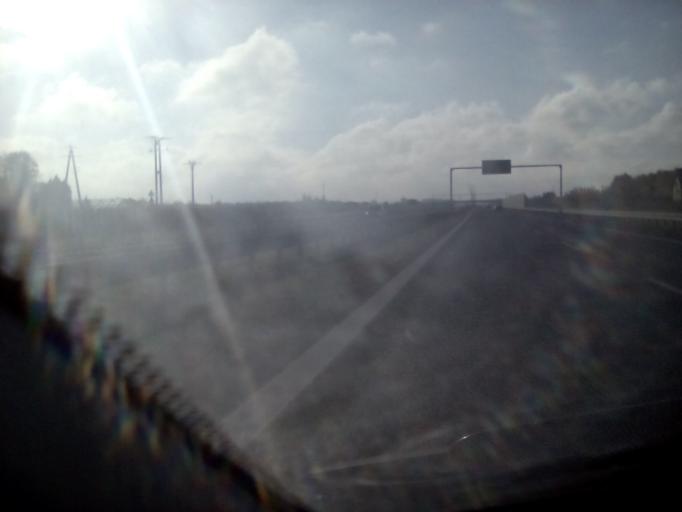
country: PL
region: Masovian Voivodeship
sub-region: Powiat grojecki
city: Goszczyn
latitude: 51.7673
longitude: 20.9012
